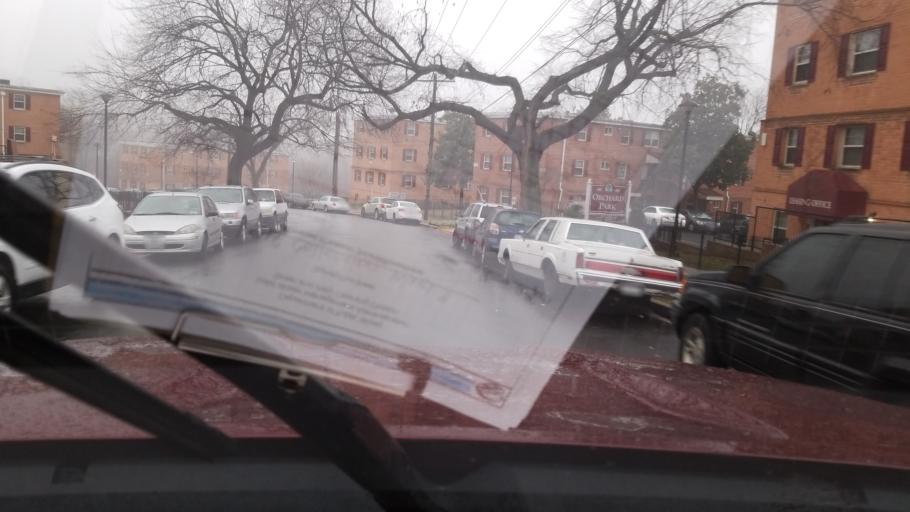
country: US
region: Maryland
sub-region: Prince George's County
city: Hillcrest Heights
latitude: 38.8456
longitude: -76.9729
